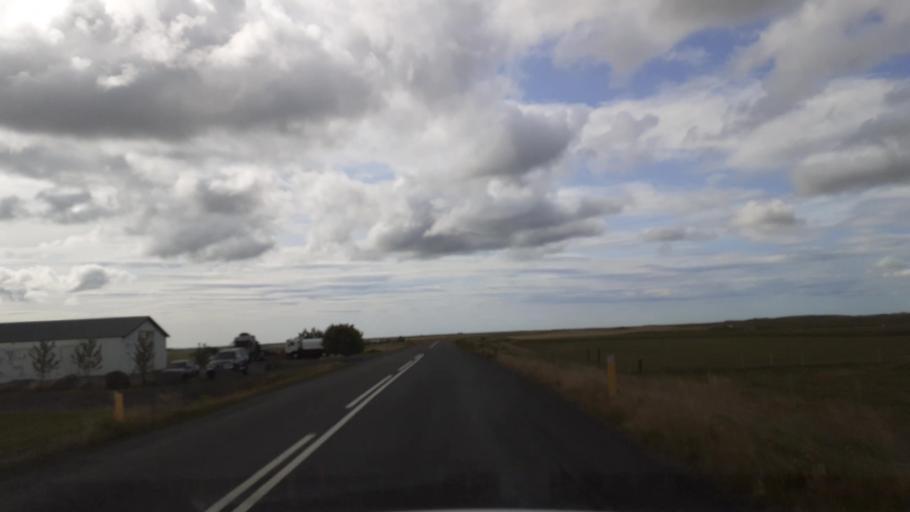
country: IS
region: South
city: Vestmannaeyjar
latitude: 63.8372
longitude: -20.4148
